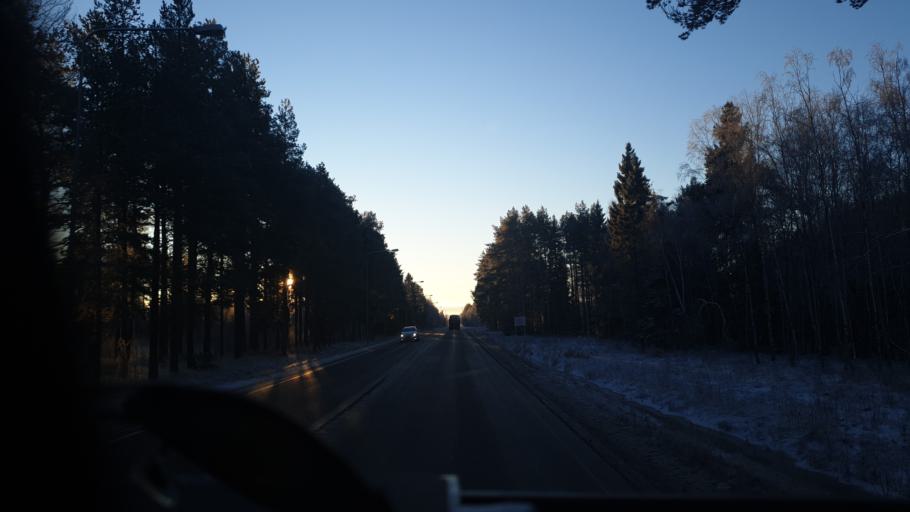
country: FI
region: Northern Ostrobothnia
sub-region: Ylivieska
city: Kalajoki
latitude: 64.2768
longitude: 23.9487
